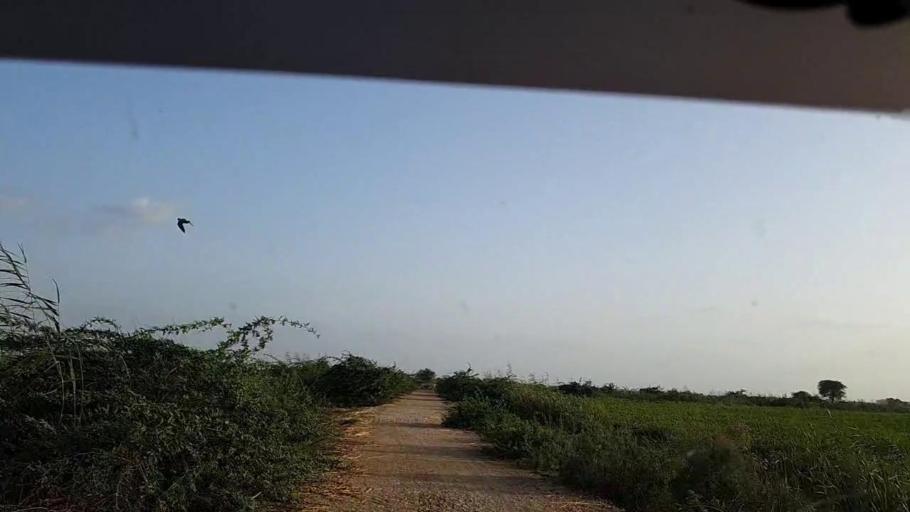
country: PK
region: Sindh
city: Kadhan
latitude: 24.5441
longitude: 68.9523
